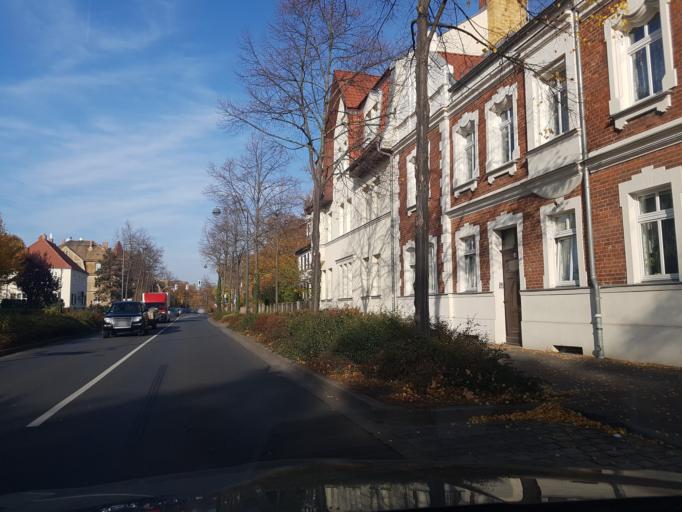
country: DE
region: Saxony
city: Torgau
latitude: 51.5549
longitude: 12.9995
